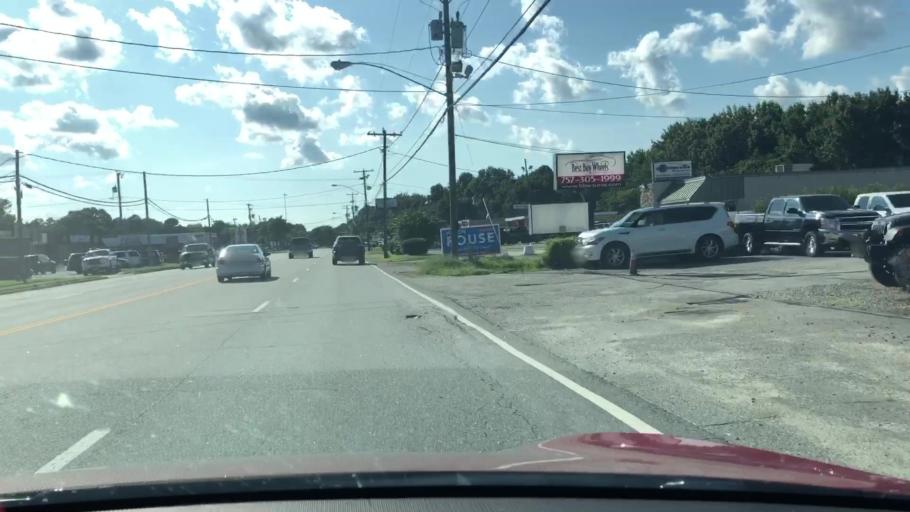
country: US
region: Virginia
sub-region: City of Virginia Beach
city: Virginia Beach
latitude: 36.8429
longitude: -76.0240
